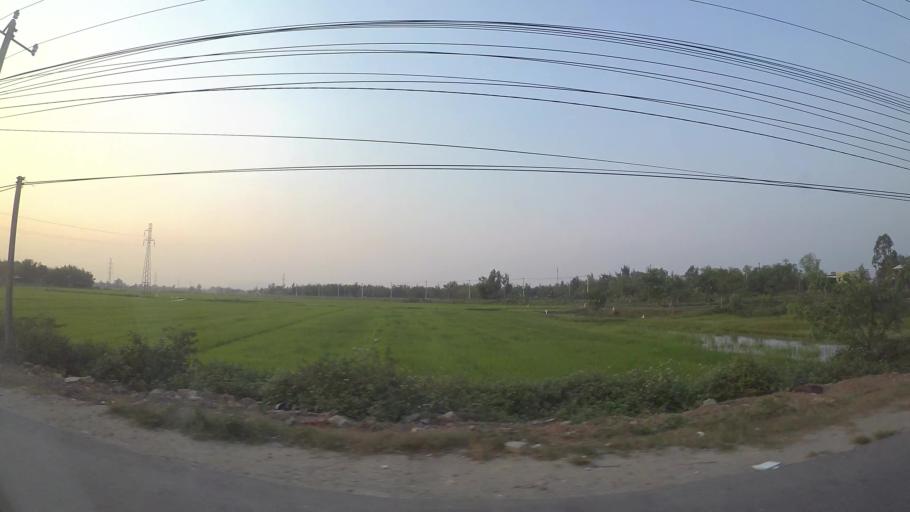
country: VN
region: Da Nang
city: Ngu Hanh Son
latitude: 15.9537
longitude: 108.2384
